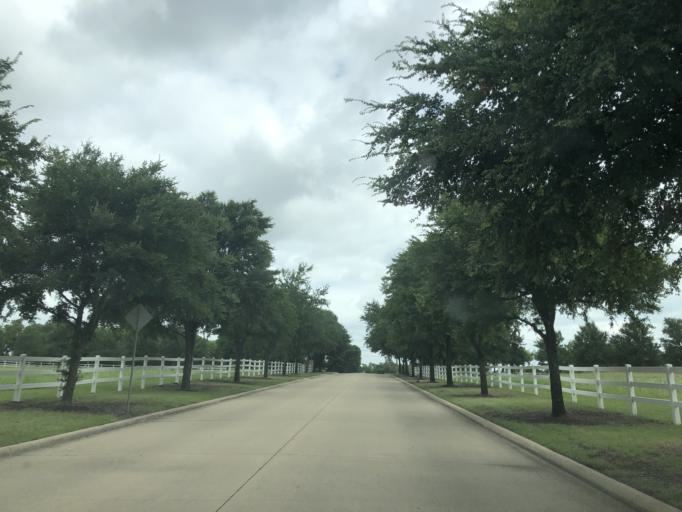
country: US
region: Texas
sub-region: Dallas County
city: Sunnyvale
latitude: 32.8127
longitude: -96.5863
